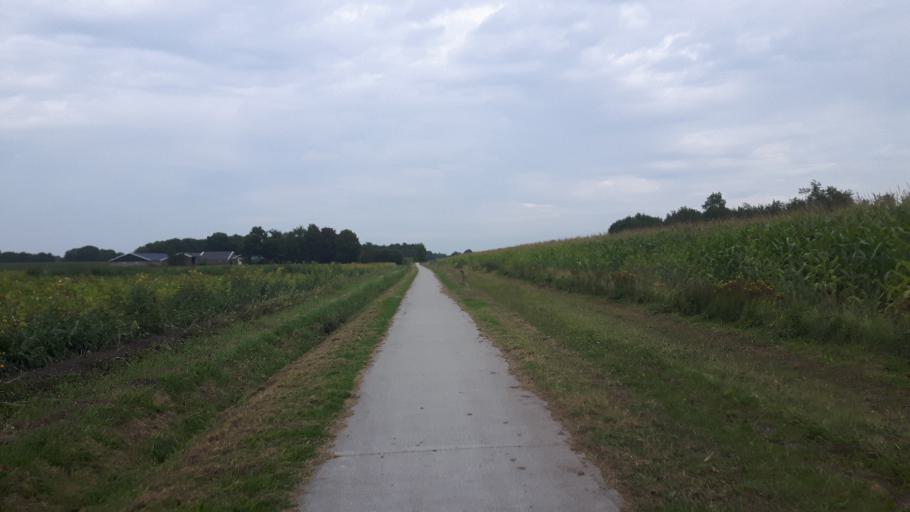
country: NL
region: Friesland
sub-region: Gemeente Weststellingwerf
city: Noordwolde
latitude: 52.9608
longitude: 6.2601
